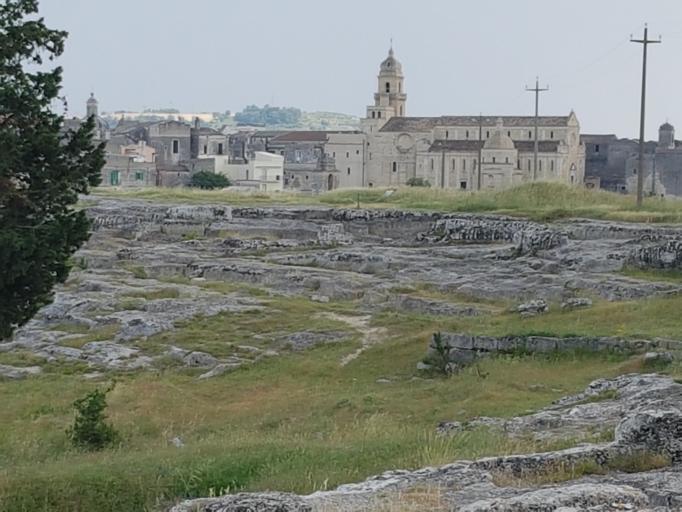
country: IT
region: Apulia
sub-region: Provincia di Bari
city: Gravina in Puglia
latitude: 40.8225
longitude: 16.4100
